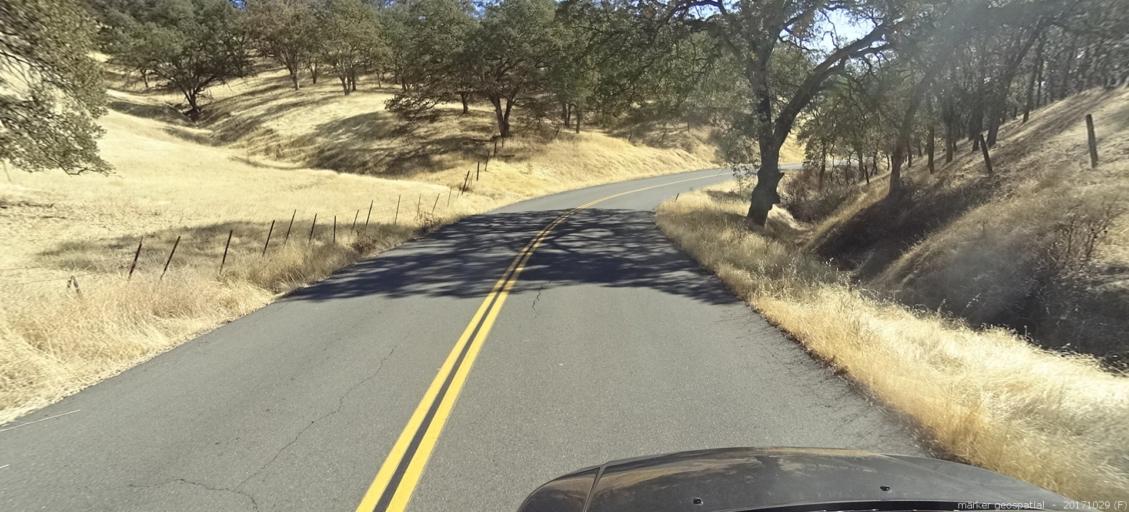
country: US
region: California
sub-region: Shasta County
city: Shasta
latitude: 40.4420
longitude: -122.6695
